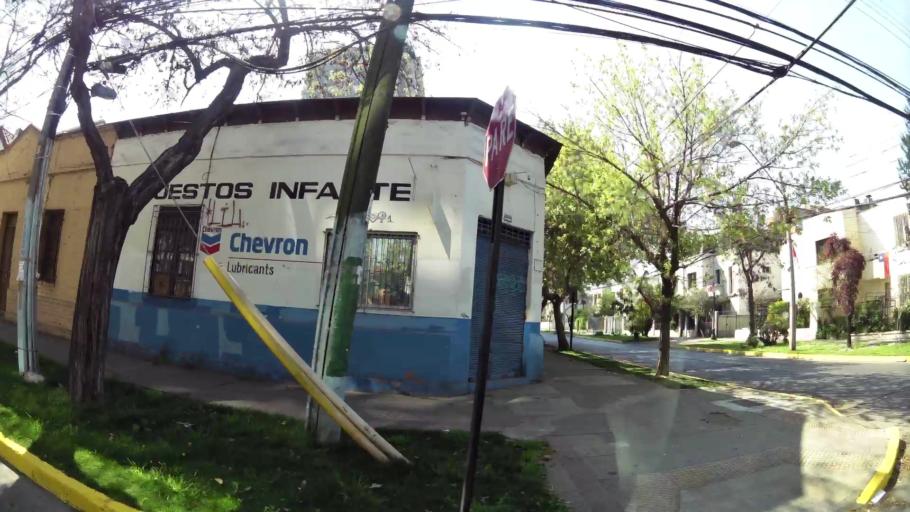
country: CL
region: Santiago Metropolitan
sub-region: Provincia de Santiago
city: Santiago
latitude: -33.4484
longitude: -70.6185
